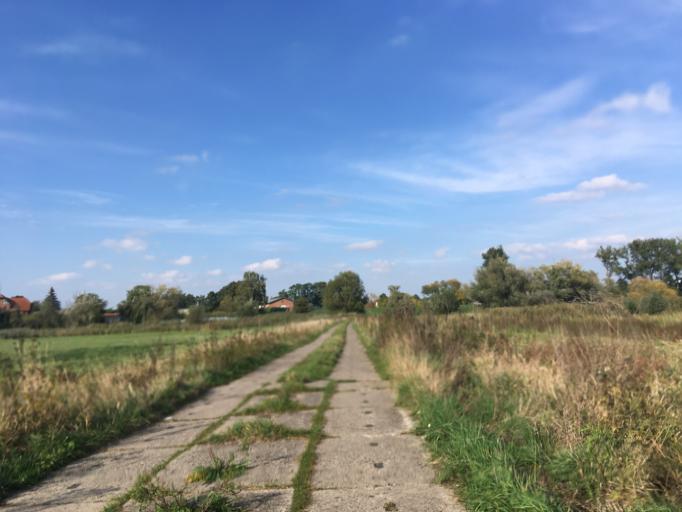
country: DE
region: Brandenburg
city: Schwedt (Oder)
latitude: 53.0446
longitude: 14.2774
